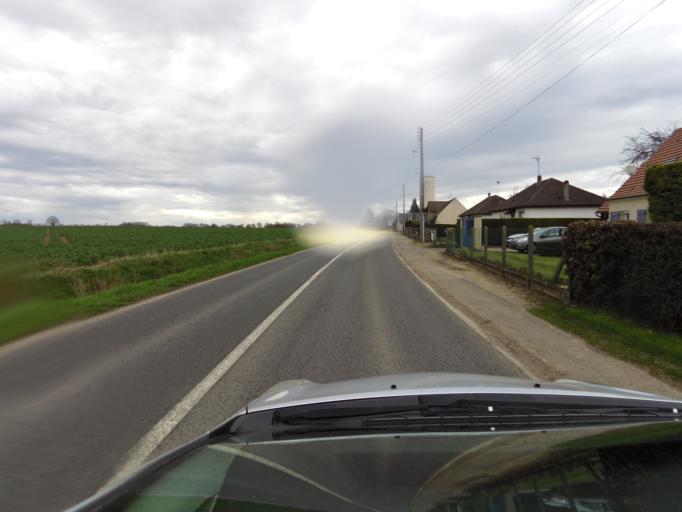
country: FR
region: Picardie
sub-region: Departement de l'Oise
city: Chamant
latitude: 49.1952
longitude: 2.6329
